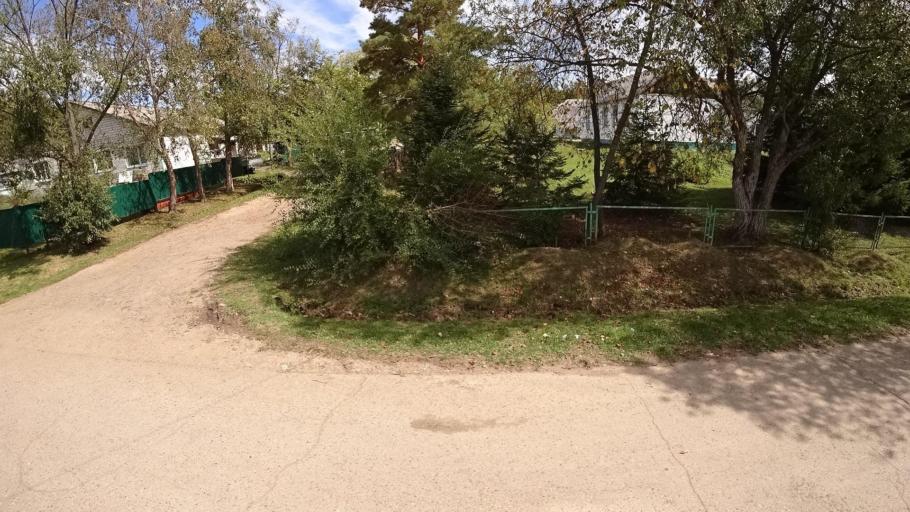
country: RU
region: Primorskiy
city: Yakovlevka
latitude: 44.6477
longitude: 133.5920
